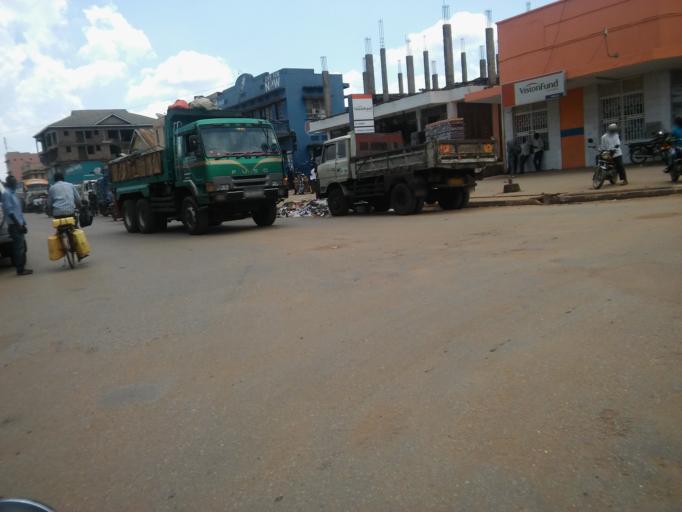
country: UG
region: Eastern Region
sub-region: Mbale District
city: Mbale
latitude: 1.0728
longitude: 34.1783
